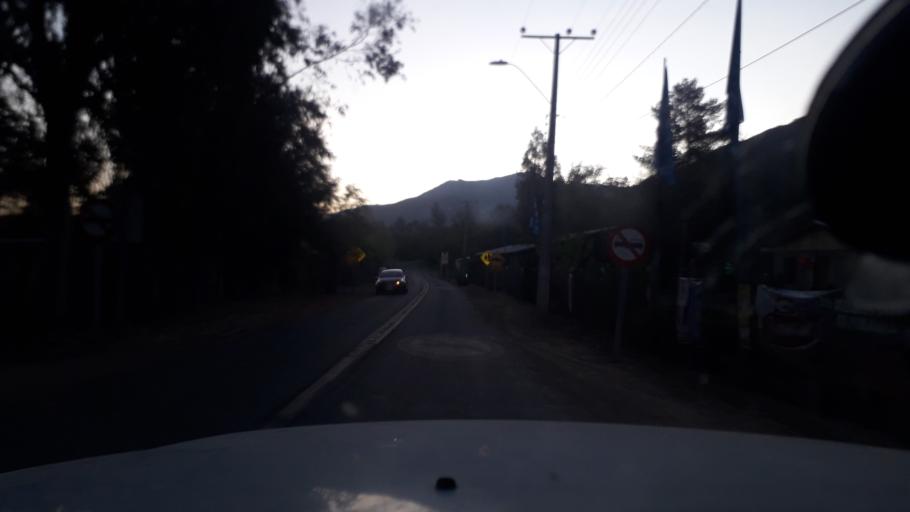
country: CL
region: Valparaiso
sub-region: Provincia de Marga Marga
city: Limache
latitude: -33.1685
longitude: -71.1424
